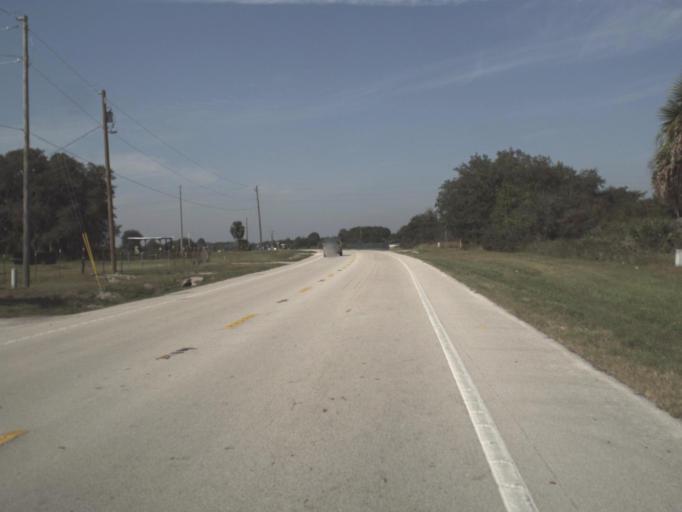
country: US
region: Florida
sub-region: Highlands County
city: Avon Park
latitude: 27.5968
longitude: -81.5375
